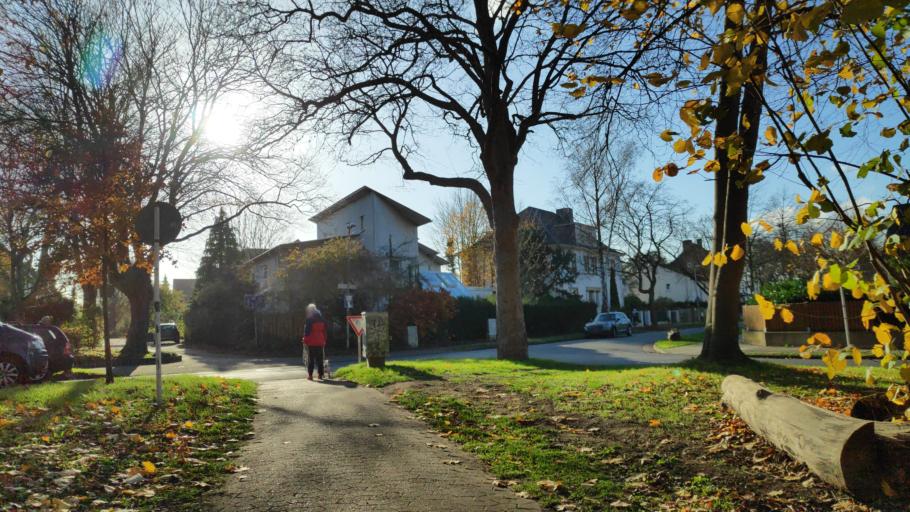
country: DE
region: North Rhine-Westphalia
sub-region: Regierungsbezirk Detmold
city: Minden
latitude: 52.2828
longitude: 8.9042
